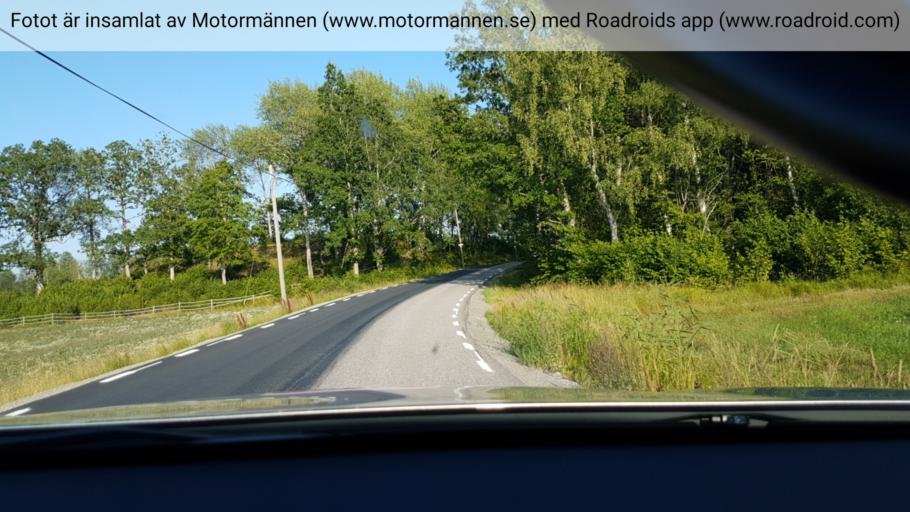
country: SE
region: Stockholm
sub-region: Nynashamns Kommun
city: Osmo
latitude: 58.9408
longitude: 17.9118
